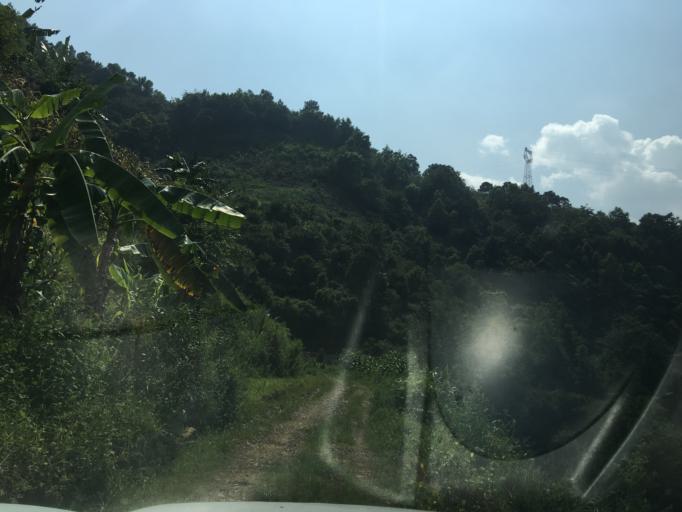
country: CN
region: Guangxi Zhuangzu Zizhiqu
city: Xinzhou
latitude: 24.9895
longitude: 105.7419
